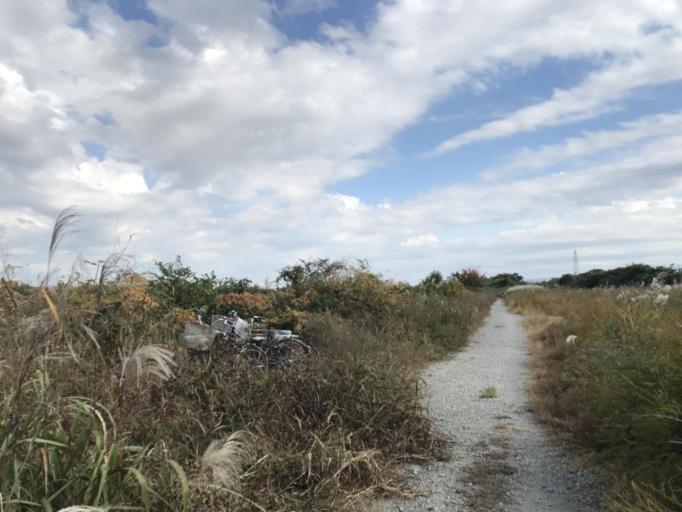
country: JP
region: Tokyo
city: Chofugaoka
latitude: 35.6196
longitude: 139.5814
